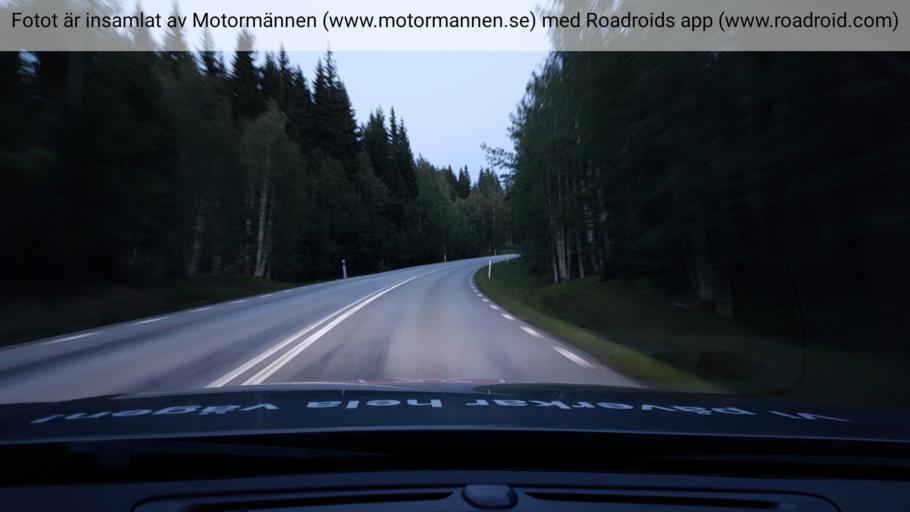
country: SE
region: OErebro
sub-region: Ljusnarsbergs Kommun
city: Kopparberg
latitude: 59.8713
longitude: 15.0358
